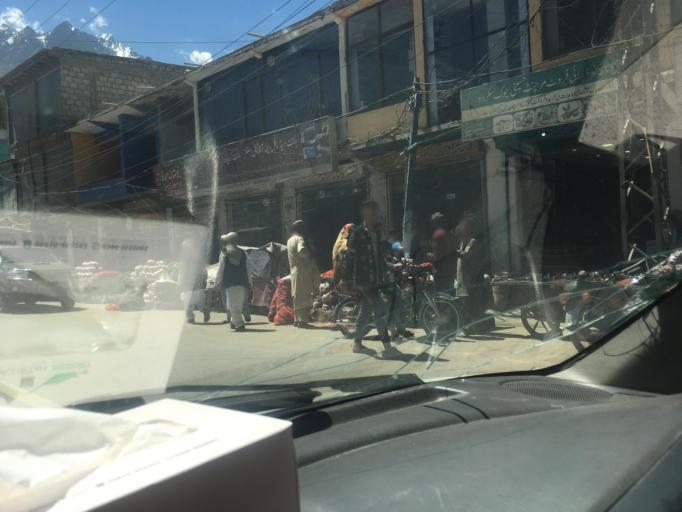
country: PK
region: Gilgit-Baltistan
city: Skardu
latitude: 35.2998
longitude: 75.6339
